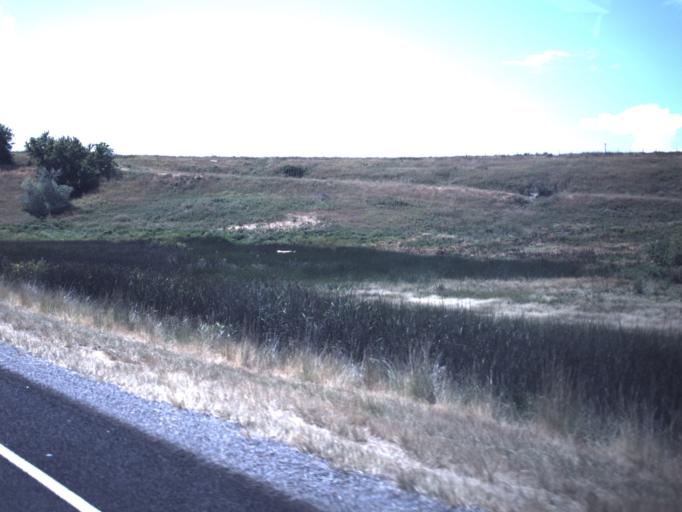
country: US
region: Utah
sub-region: Box Elder County
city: Garland
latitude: 41.8357
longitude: -112.1467
